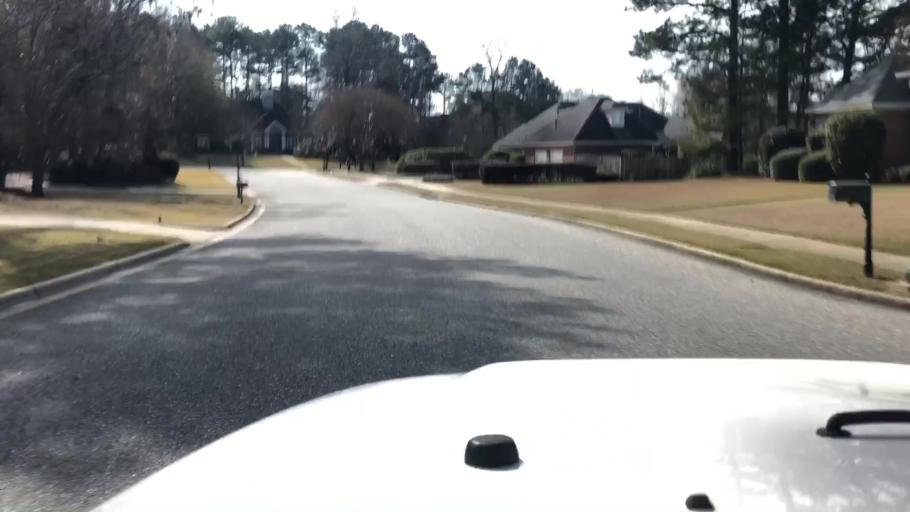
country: US
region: Alabama
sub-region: Montgomery County
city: Pike Road
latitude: 32.3569
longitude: -86.1486
